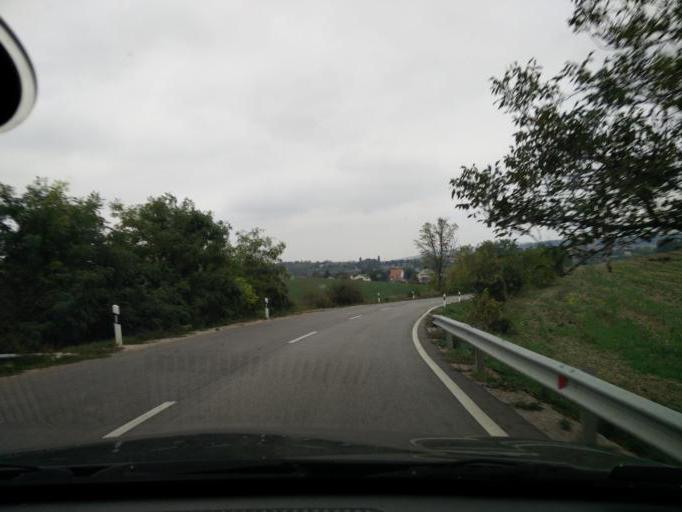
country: HU
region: Komarom-Esztergom
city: Bajna
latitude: 47.6740
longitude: 18.6052
